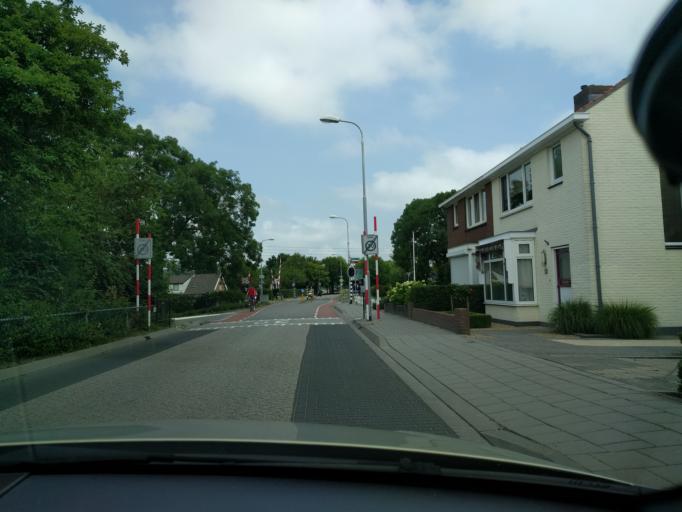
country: NL
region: Zeeland
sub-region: Gemeente Veere
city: Veere
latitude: 51.5016
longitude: 3.6773
